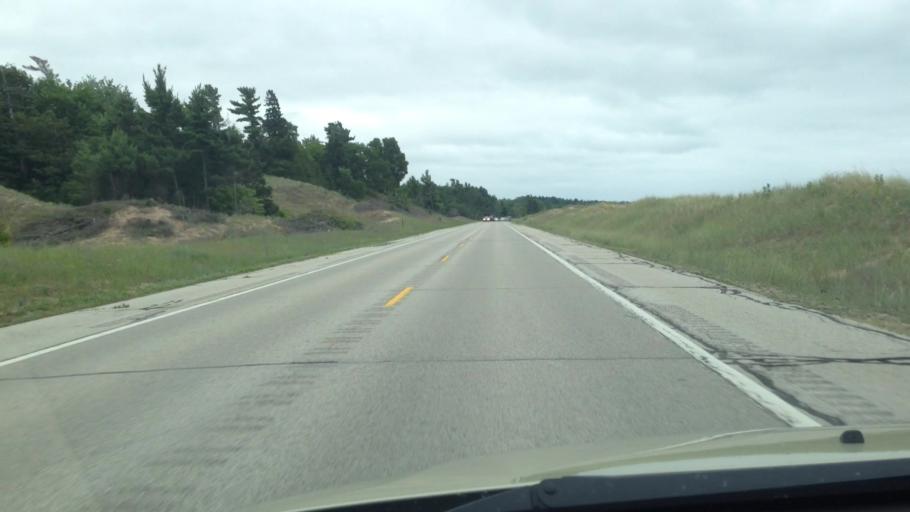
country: US
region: Michigan
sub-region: Mackinac County
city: Saint Ignace
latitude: 45.9629
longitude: -84.9435
